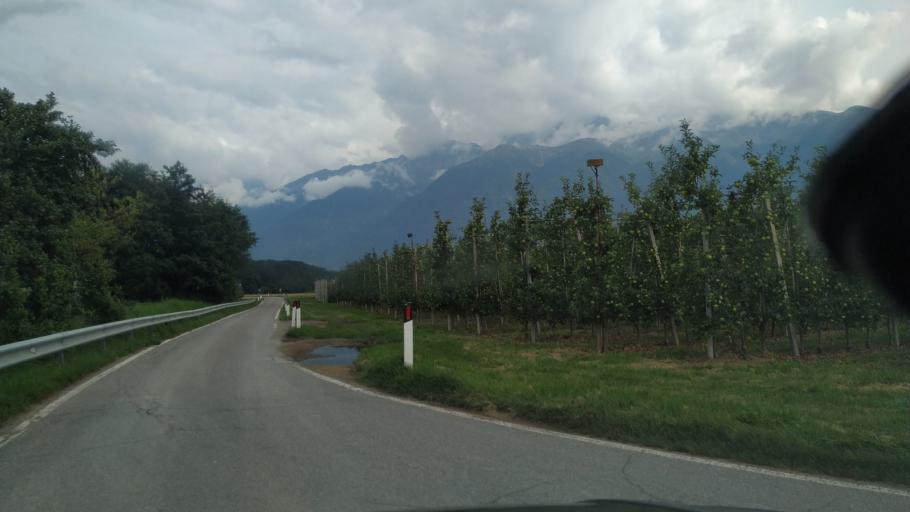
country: IT
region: Trentino-Alto Adige
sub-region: Bolzano
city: Sluderno
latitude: 46.6561
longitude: 10.5756
